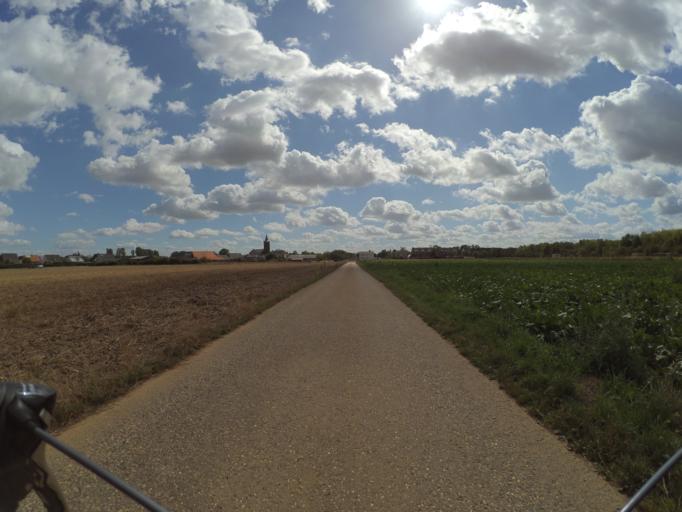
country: DE
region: North Rhine-Westphalia
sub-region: Regierungsbezirk Koln
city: Inden
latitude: 50.8782
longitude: 6.3921
